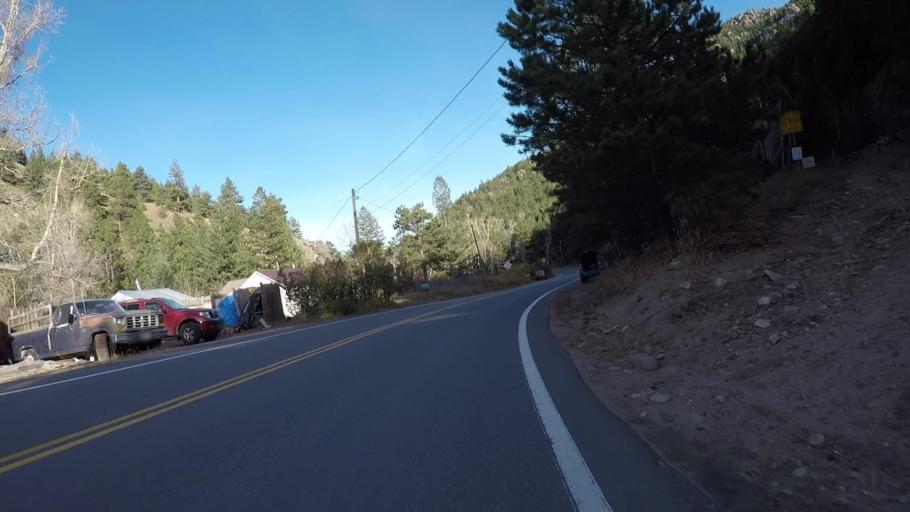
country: US
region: Colorado
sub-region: Boulder County
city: Boulder
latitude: 40.0782
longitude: -105.3861
